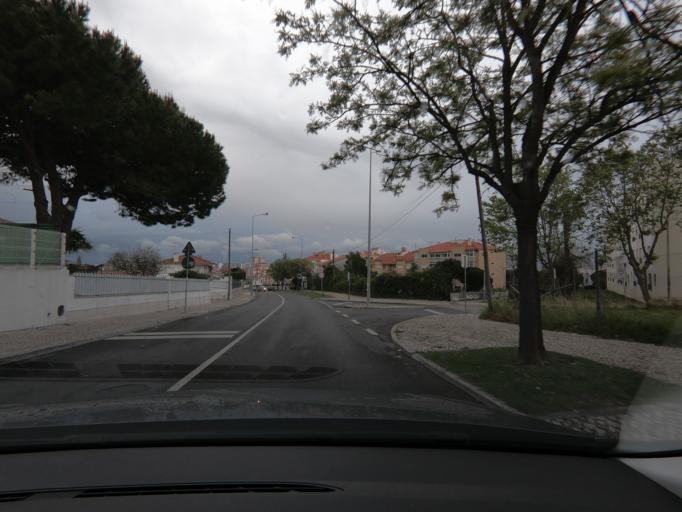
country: PT
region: Lisbon
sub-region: Cascais
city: Sao Domingos de Rana
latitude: 38.7001
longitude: -9.3374
